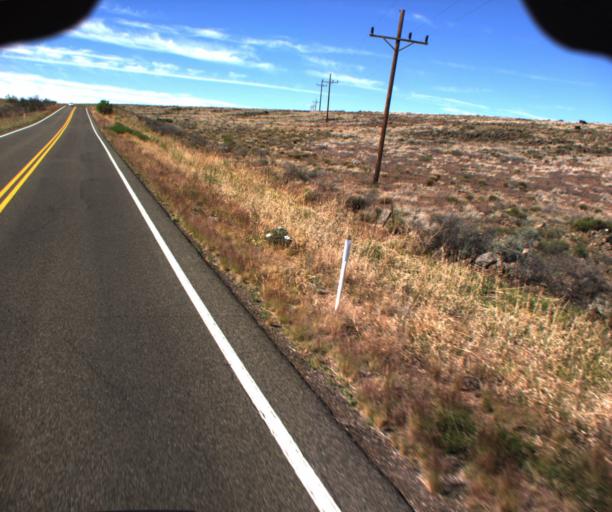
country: US
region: Arizona
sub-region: Yavapai County
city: Congress
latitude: 34.3382
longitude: -112.6862
